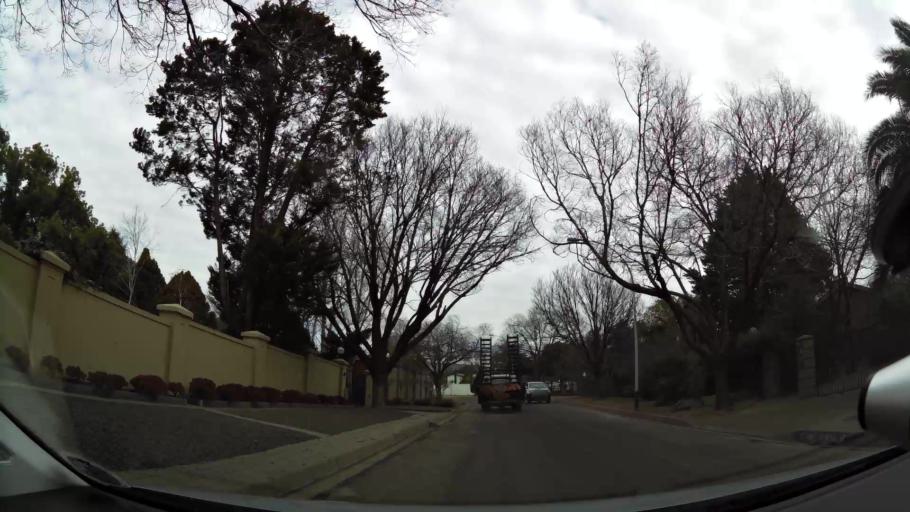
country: ZA
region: Orange Free State
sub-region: Mangaung Metropolitan Municipality
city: Bloemfontein
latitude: -29.0959
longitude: 26.2121
